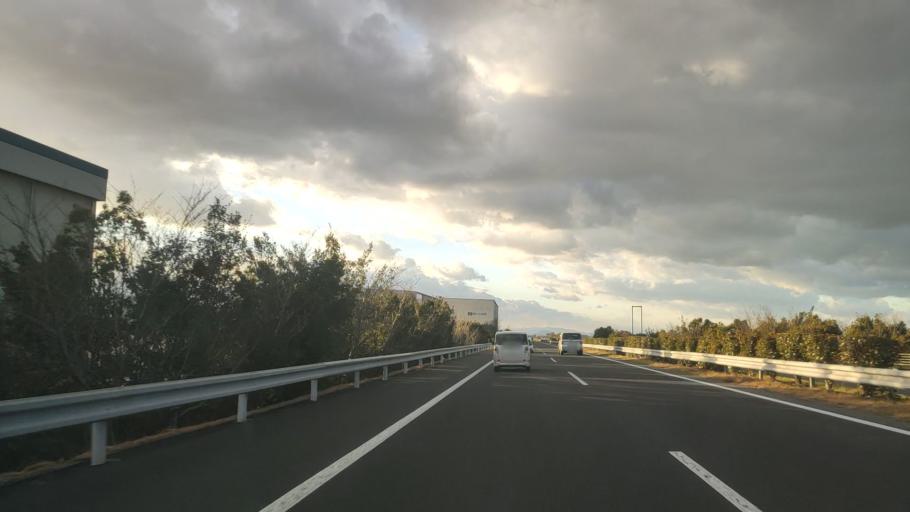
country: JP
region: Ehime
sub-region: Shikoku-chuo Shi
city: Matsuyama
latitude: 33.7861
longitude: 132.8399
